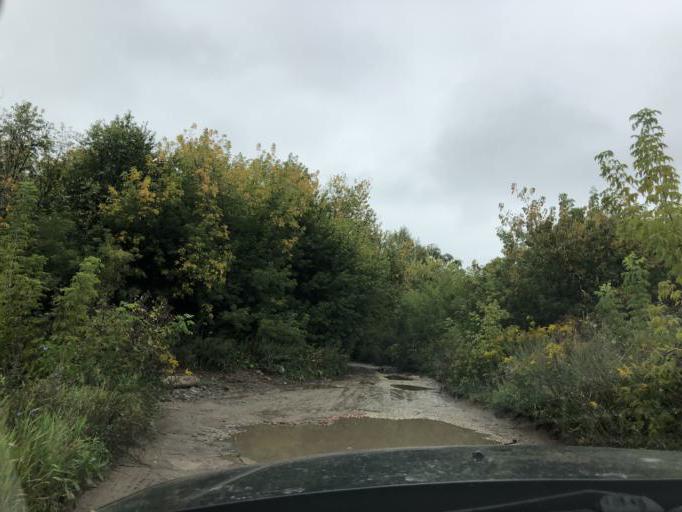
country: RU
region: Tula
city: Mendeleyevskiy
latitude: 54.1687
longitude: 37.5511
